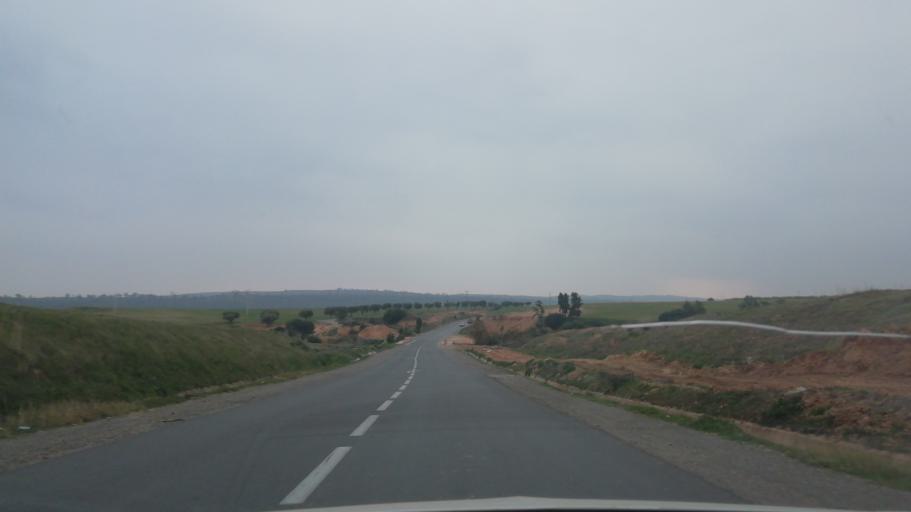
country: DZ
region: Sidi Bel Abbes
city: Sfizef
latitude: 35.2751
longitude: -0.1552
